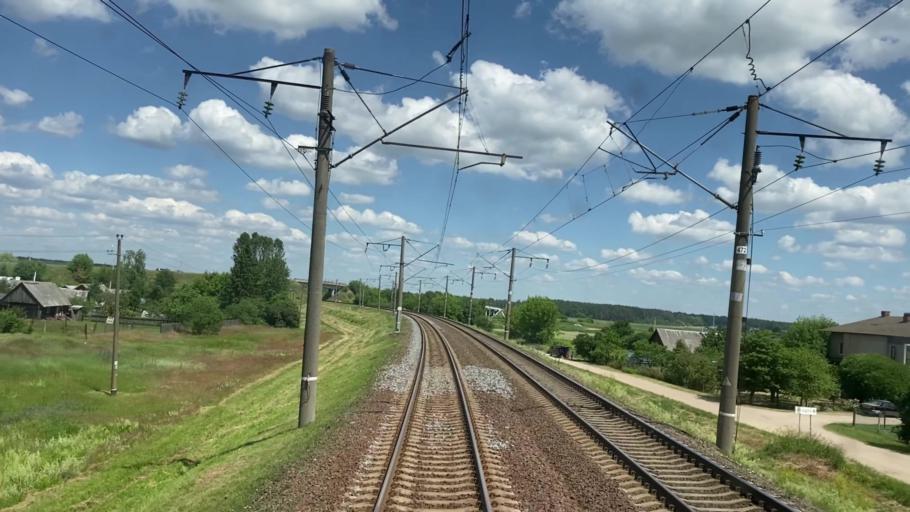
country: BY
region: Brest
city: Ivatsevichy
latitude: 52.7145
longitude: 25.3548
